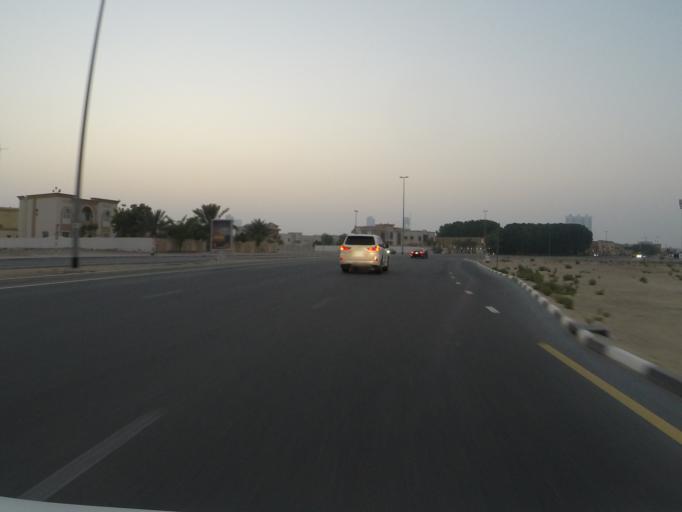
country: AE
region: Dubai
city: Dubai
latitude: 25.0974
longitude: 55.2013
